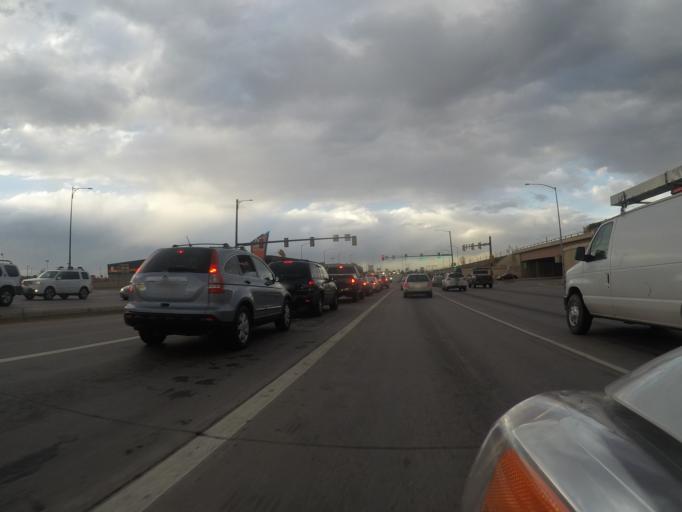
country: US
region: Colorado
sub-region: Arapahoe County
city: Englewood
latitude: 39.6416
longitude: -105.0060
